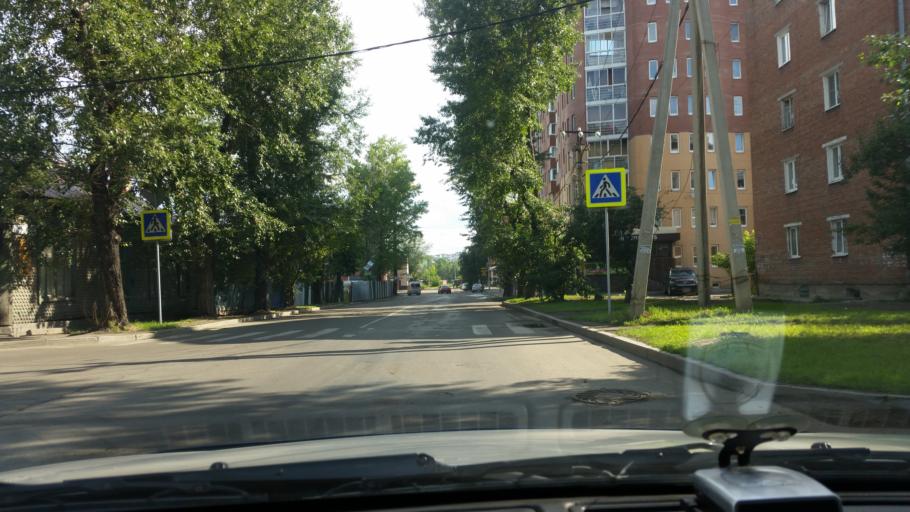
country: RU
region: Irkutsk
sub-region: Irkutskiy Rayon
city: Irkutsk
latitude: 52.2870
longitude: 104.3087
